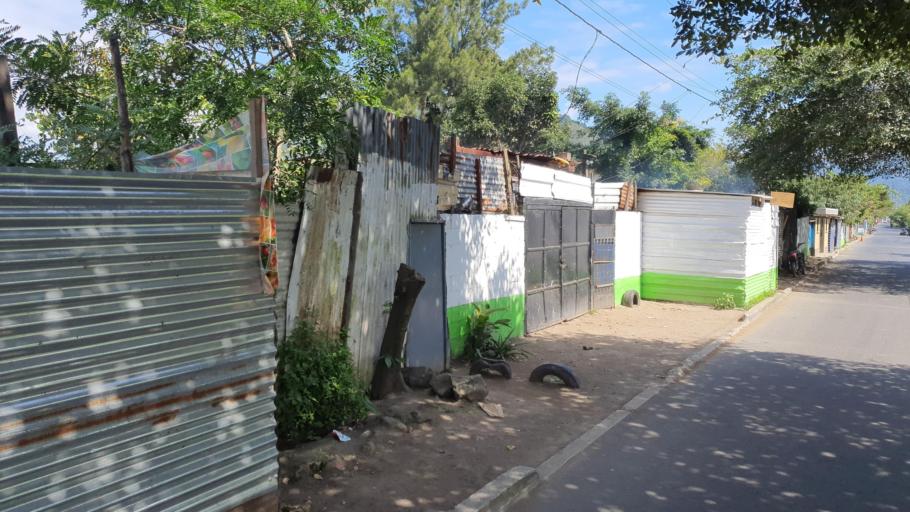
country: GT
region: Guatemala
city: Villa Canales
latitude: 14.4617
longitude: -90.5538
